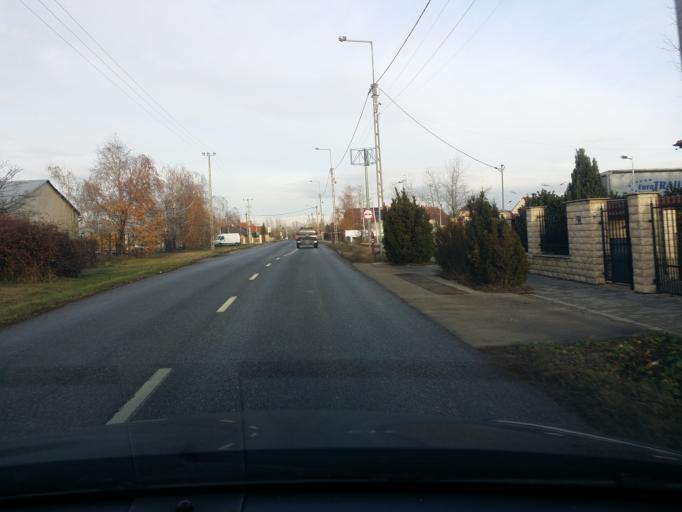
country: HU
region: Pest
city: Alsonemedi
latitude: 47.3241
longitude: 19.1483
